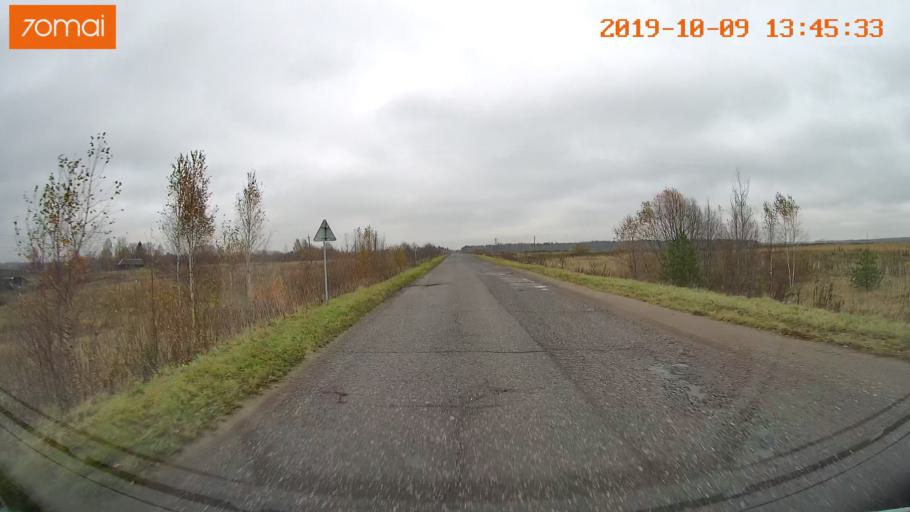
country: RU
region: Kostroma
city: Buy
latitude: 58.3752
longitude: 41.2108
